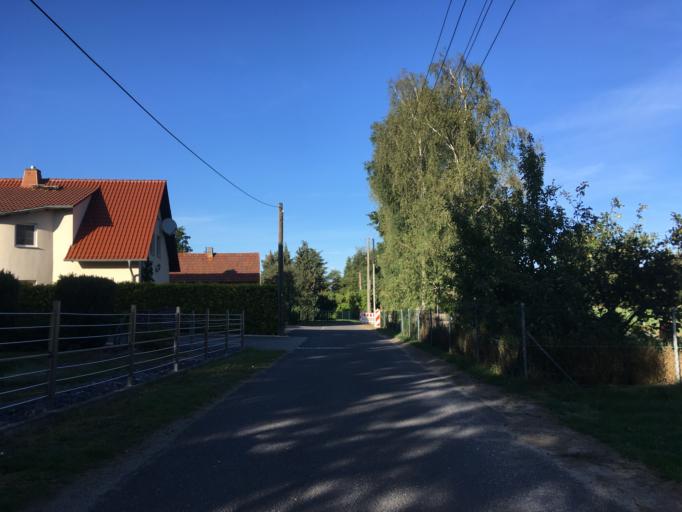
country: DE
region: Saxony
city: Bad Muskau
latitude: 51.5679
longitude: 14.7147
